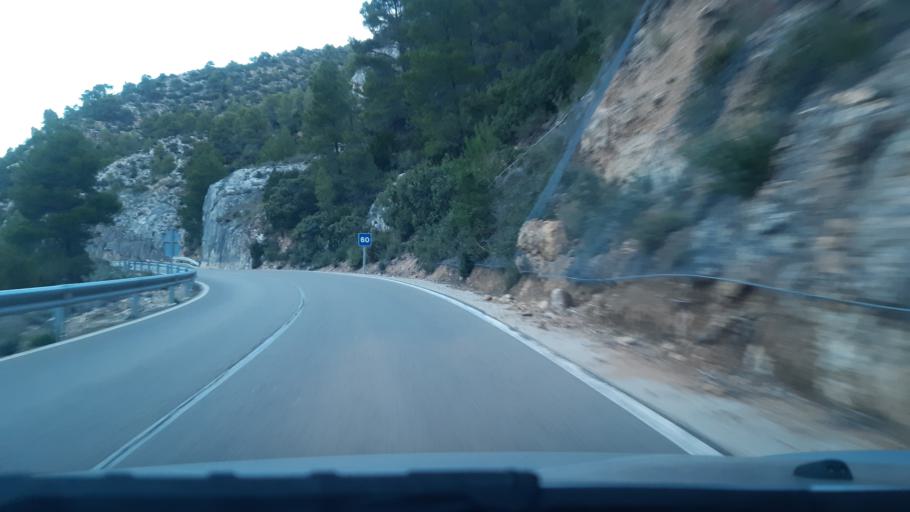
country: ES
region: Aragon
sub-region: Provincia de Teruel
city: Valderrobres
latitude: 40.8421
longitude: 0.1765
